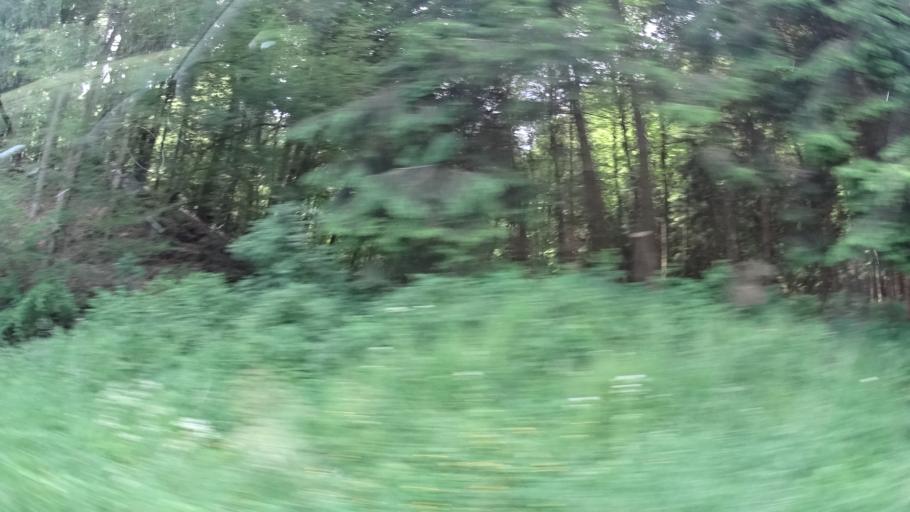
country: DE
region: Bavaria
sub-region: Regierungsbezirk Unterfranken
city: Hasloch
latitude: 49.8037
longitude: 9.4957
